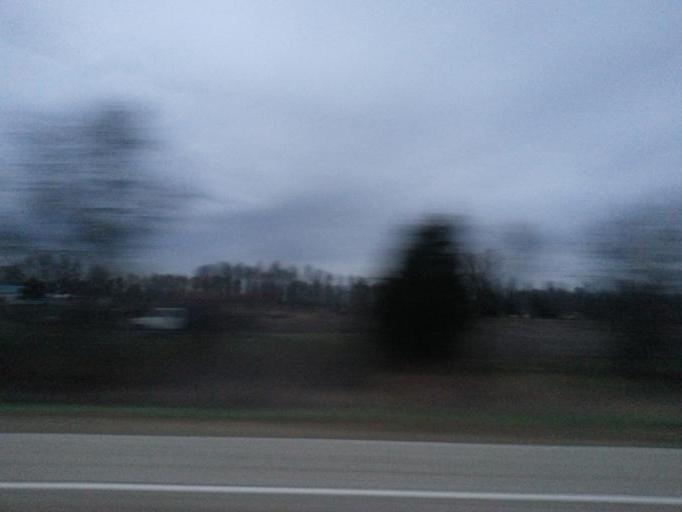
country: US
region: Iowa
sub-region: Black Hawk County
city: Elk Run Heights
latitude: 42.4504
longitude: -92.2273
